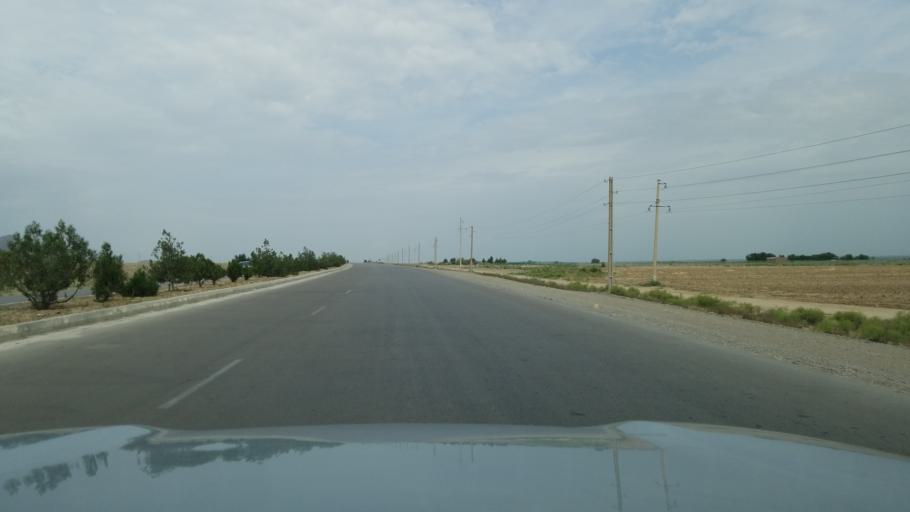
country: TM
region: Ahal
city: Baharly
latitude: 38.2262
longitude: 57.7937
